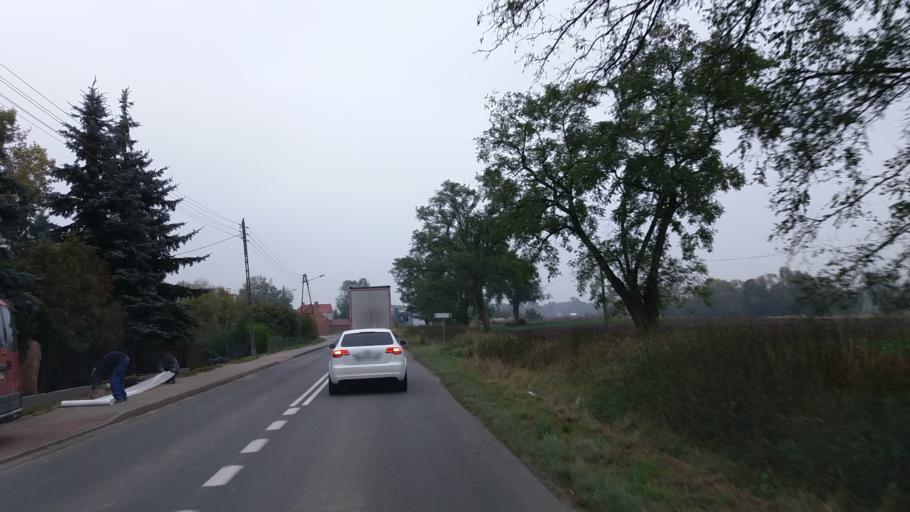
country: PL
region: West Pomeranian Voivodeship
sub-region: Powiat choszczenski
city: Bierzwnik
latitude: 53.0474
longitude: 15.6661
